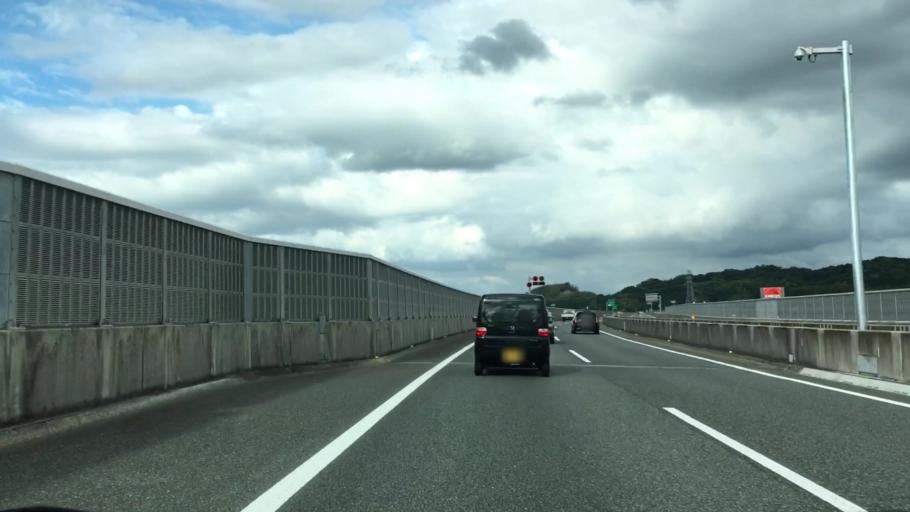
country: JP
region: Fukuoka
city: Maebaru-chuo
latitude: 33.5635
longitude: 130.2362
